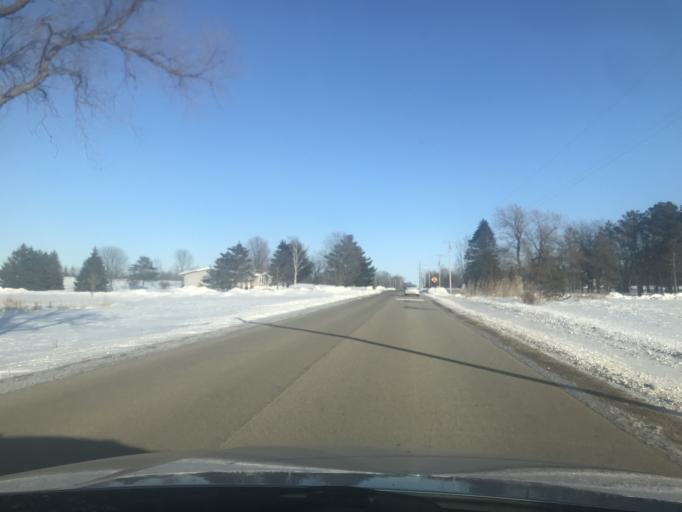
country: US
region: Wisconsin
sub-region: Marinette County
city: Marinette
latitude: 45.1450
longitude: -87.6587
